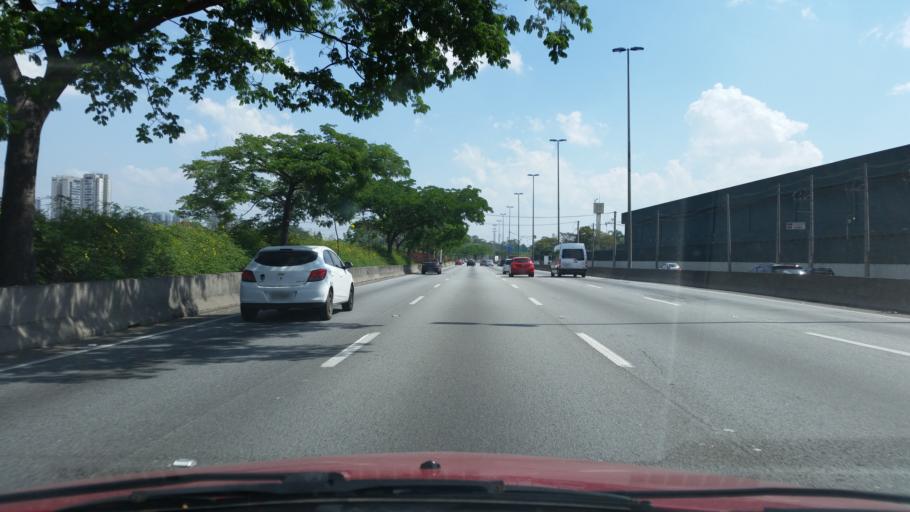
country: BR
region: Sao Paulo
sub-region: Osasco
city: Osasco
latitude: -23.5153
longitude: -46.7283
